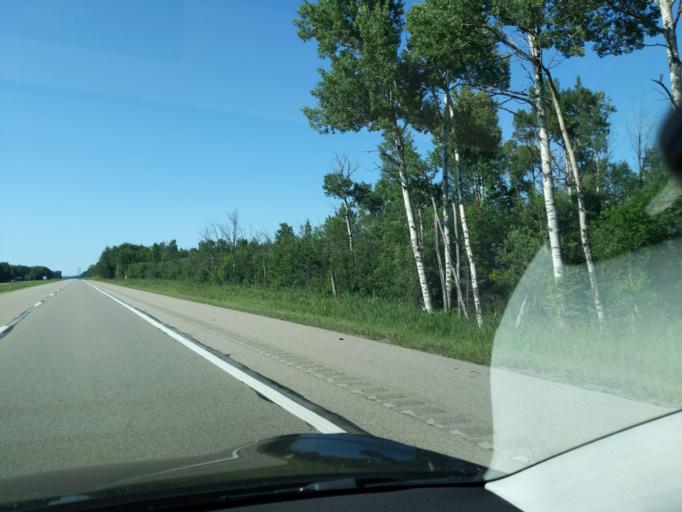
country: US
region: Michigan
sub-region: Mackinac County
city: Saint Ignace
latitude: 45.7380
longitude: -84.7284
